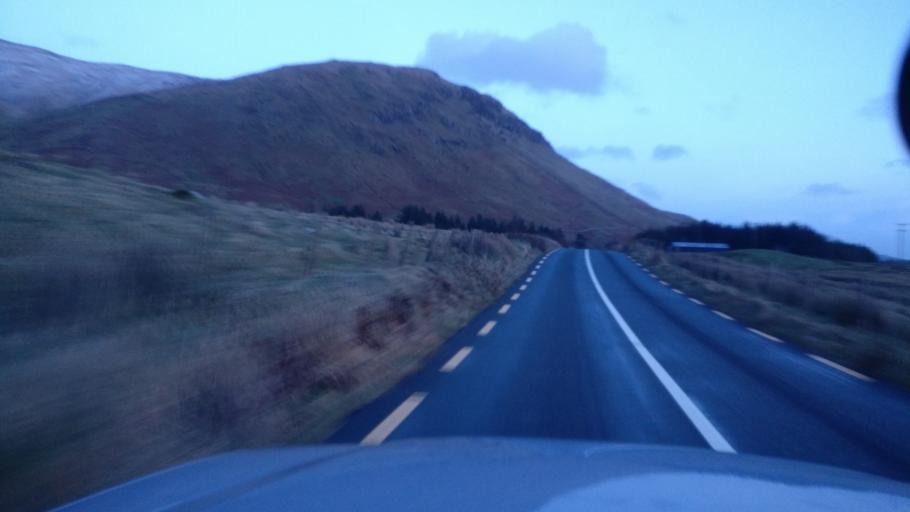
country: IE
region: Connaught
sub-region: Maigh Eo
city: Westport
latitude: 53.5492
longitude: -9.6307
